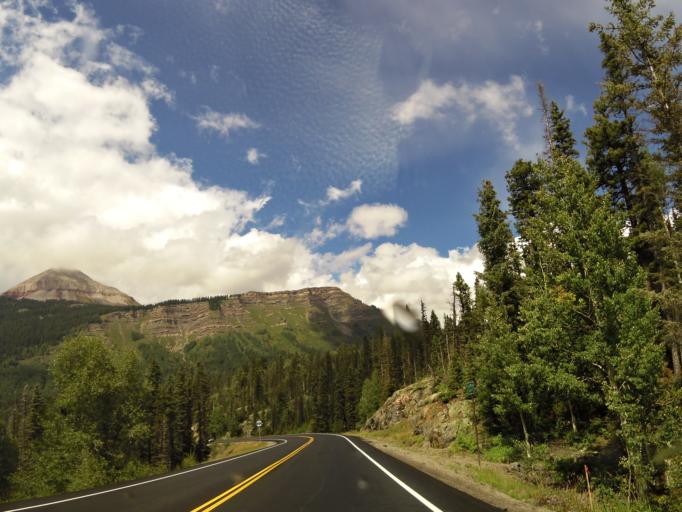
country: US
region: Colorado
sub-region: San Juan County
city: Silverton
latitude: 37.6760
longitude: -107.7820
